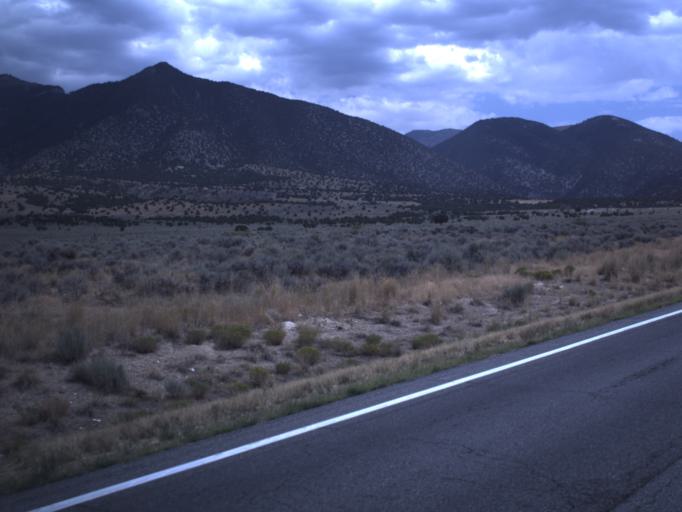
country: US
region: Utah
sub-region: Tooele County
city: Tooele
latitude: 40.3583
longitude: -112.3217
